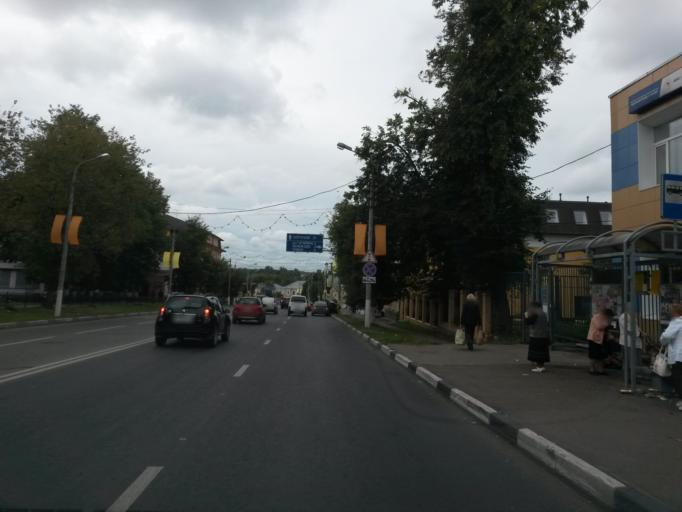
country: RU
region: Moskovskaya
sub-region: Chekhovskiy Rayon
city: Chekhov
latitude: 55.1456
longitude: 37.4543
